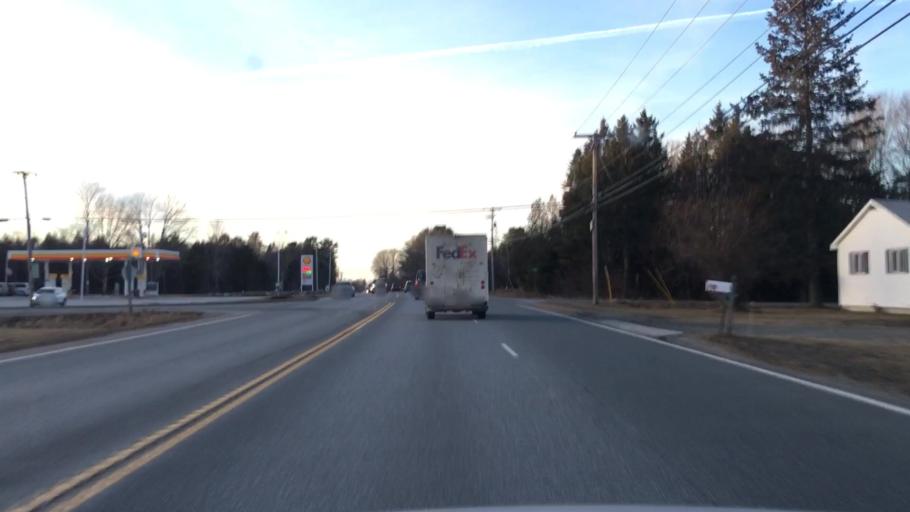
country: US
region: Maine
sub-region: Penobscot County
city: Holden
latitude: 44.7494
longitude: -68.6485
